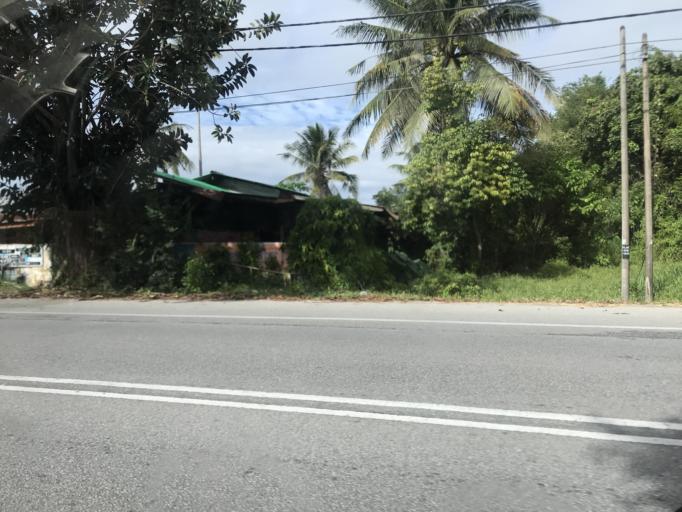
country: MY
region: Kelantan
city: Kota Bharu
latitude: 6.1248
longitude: 102.1824
